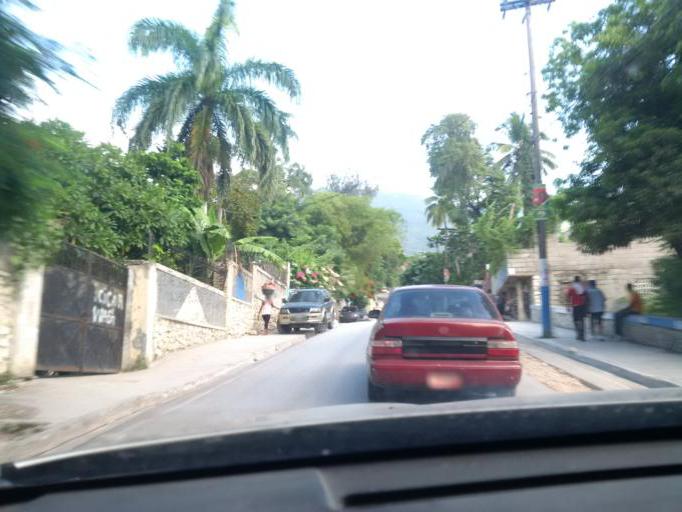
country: HT
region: Ouest
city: Port-au-Prince
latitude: 18.5293
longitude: -72.3221
